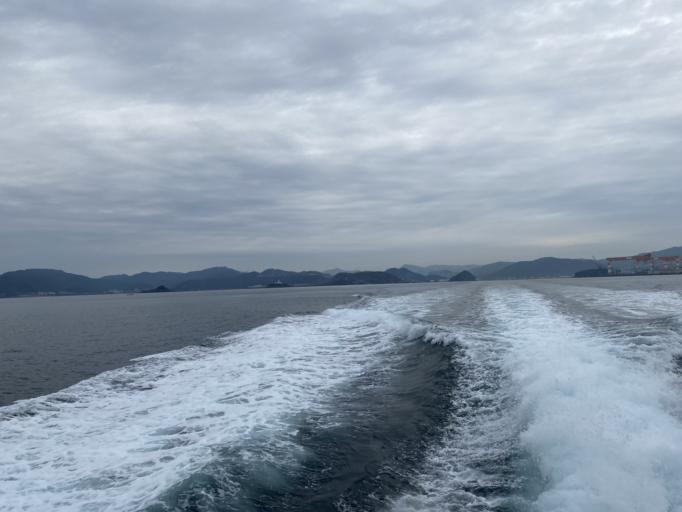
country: JP
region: Nagasaki
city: Nagasaki-shi
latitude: 32.7038
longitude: 129.7881
